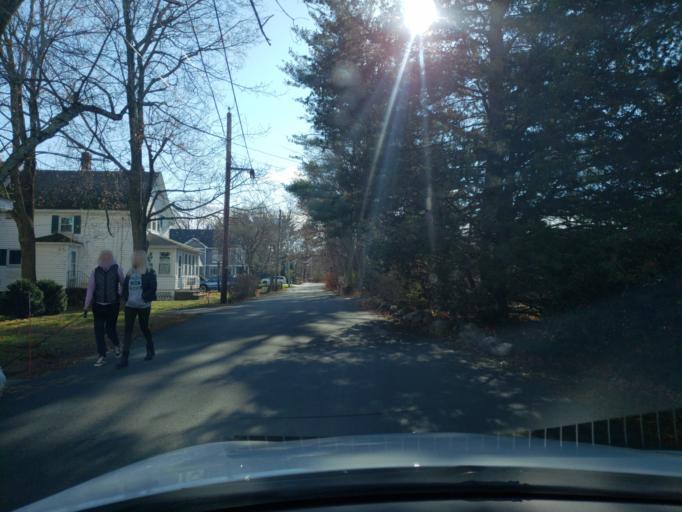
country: US
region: Massachusetts
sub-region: Essex County
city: Andover
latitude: 42.6589
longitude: -71.1300
